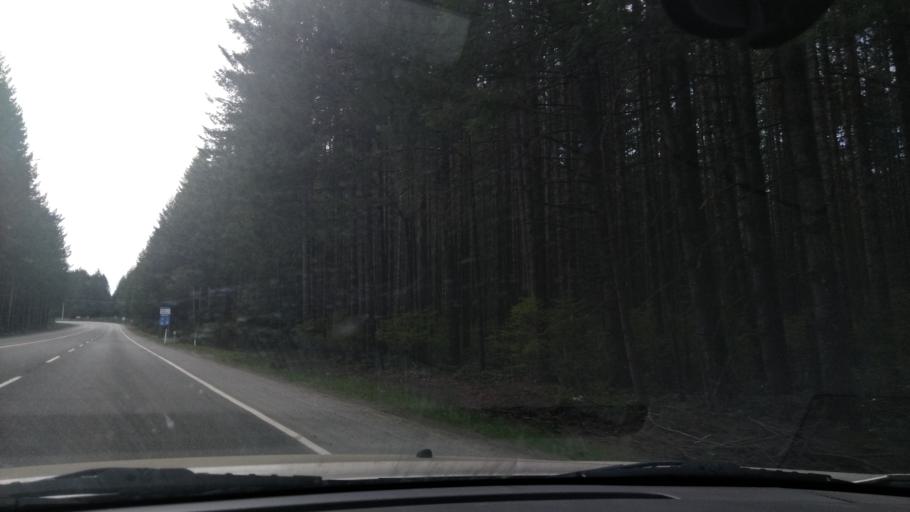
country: CA
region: British Columbia
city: Campbell River
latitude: 50.0362
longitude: -125.3233
